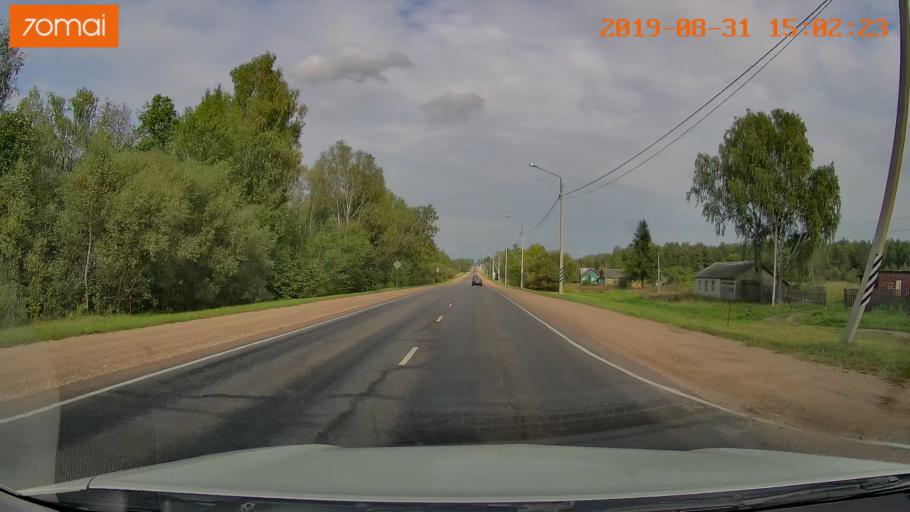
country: RU
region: Kaluga
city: Spas-Demensk
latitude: 54.3453
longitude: 34.0735
